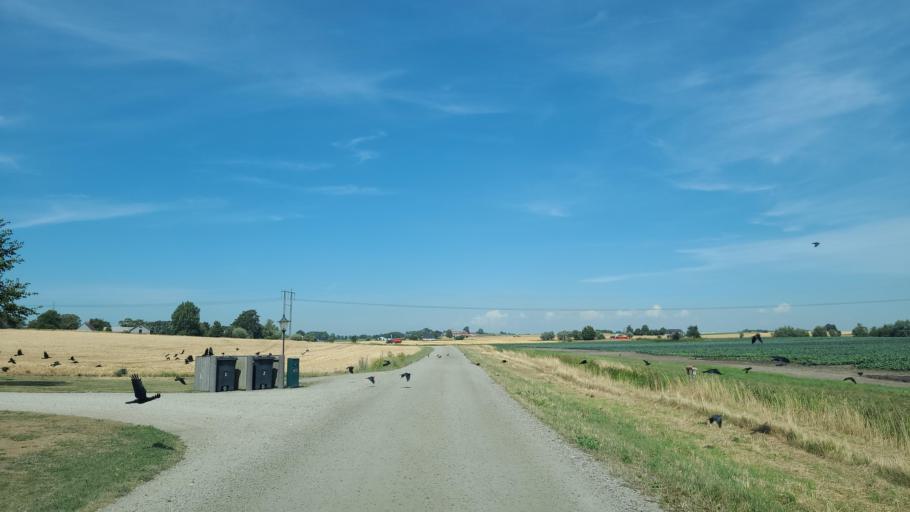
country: SE
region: Skane
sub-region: Trelleborgs Kommun
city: Skare
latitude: 55.4168
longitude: 13.0658
